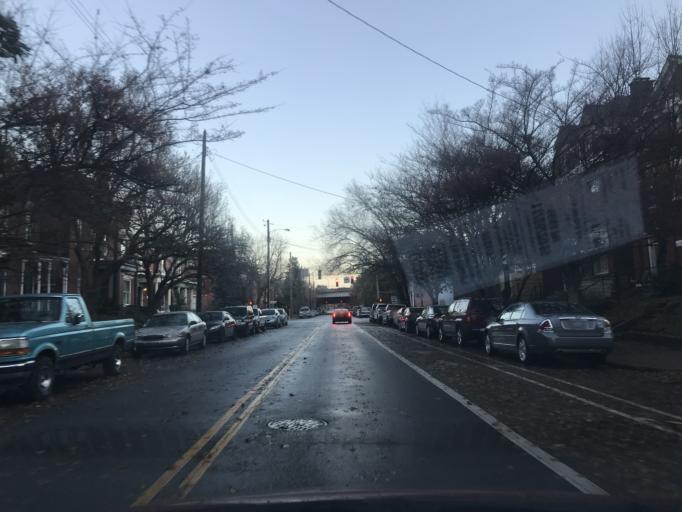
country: US
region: Kentucky
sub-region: Jefferson County
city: Louisville
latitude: 38.2360
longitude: -85.7534
